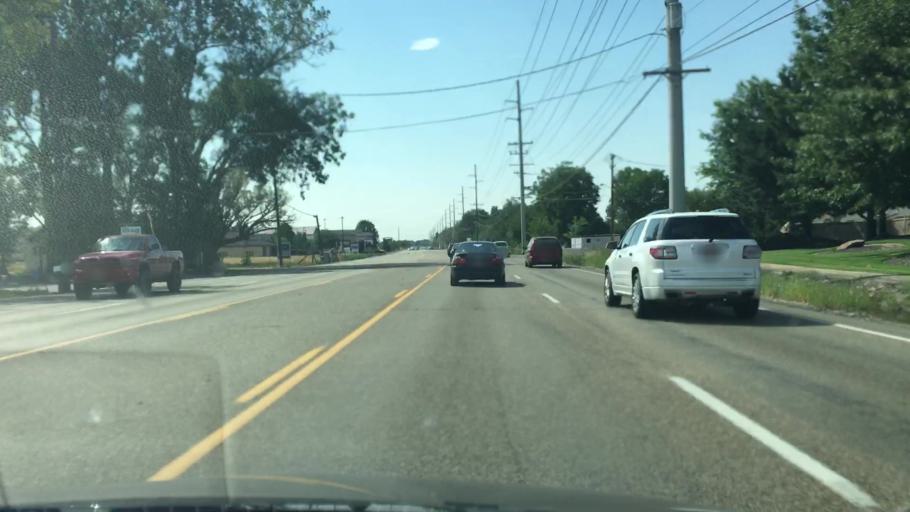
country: US
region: Idaho
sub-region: Ada County
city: Eagle
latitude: 43.6781
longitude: -116.3007
